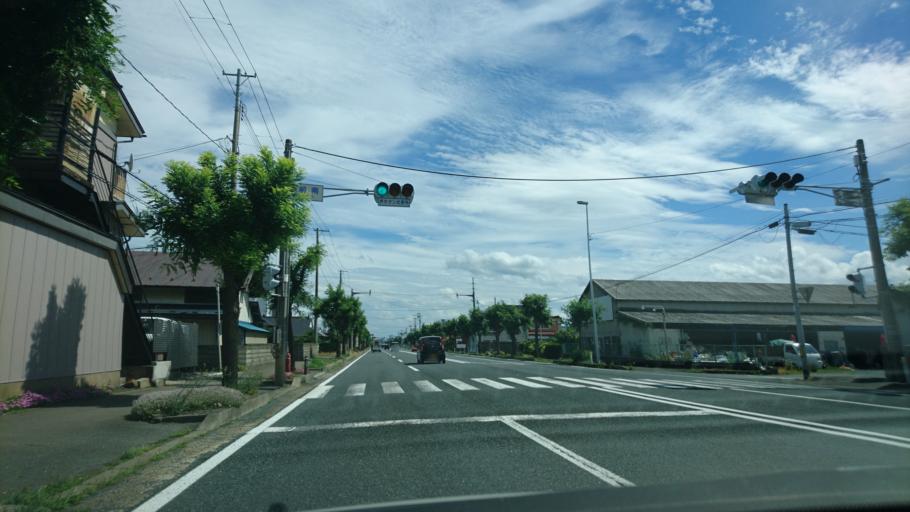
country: JP
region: Iwate
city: Morioka-shi
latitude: 39.6341
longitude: 141.1730
